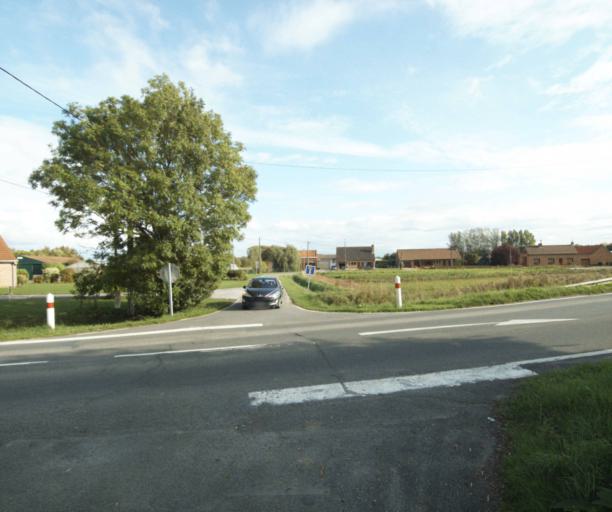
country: FR
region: Nord-Pas-de-Calais
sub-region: Departement du Nord
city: Radinghem-en-Weppes
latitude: 50.6469
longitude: 2.9086
